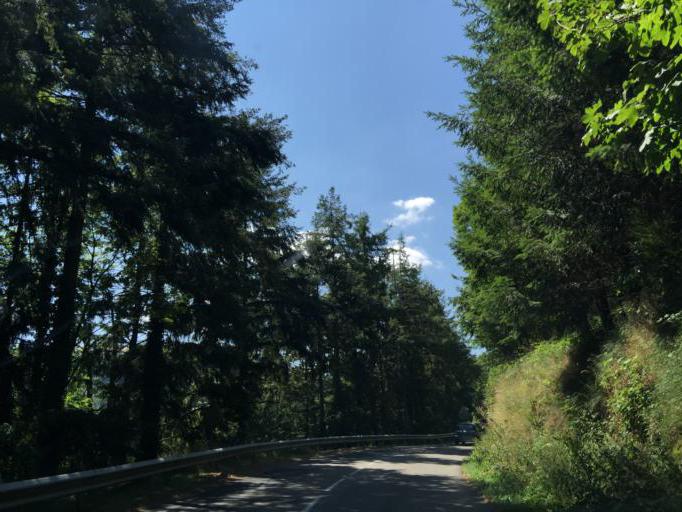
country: FR
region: Rhone-Alpes
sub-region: Departement de la Loire
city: Saint-Chamond
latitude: 45.4305
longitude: 4.5141
